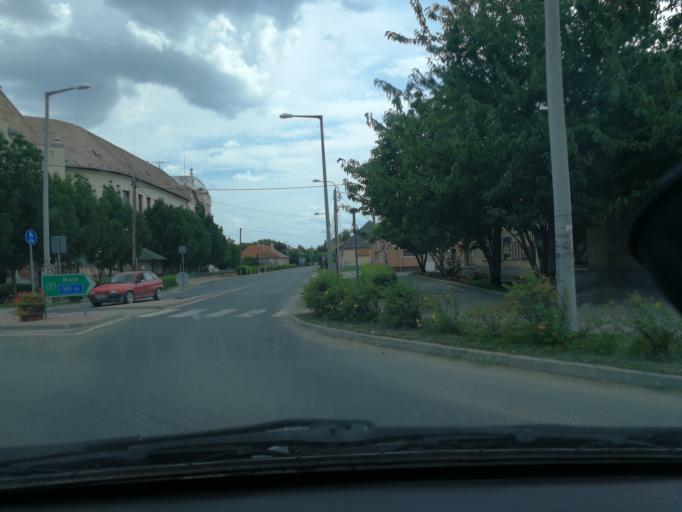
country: HU
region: Bacs-Kiskun
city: Dunapataj
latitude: 46.6442
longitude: 19.0001
